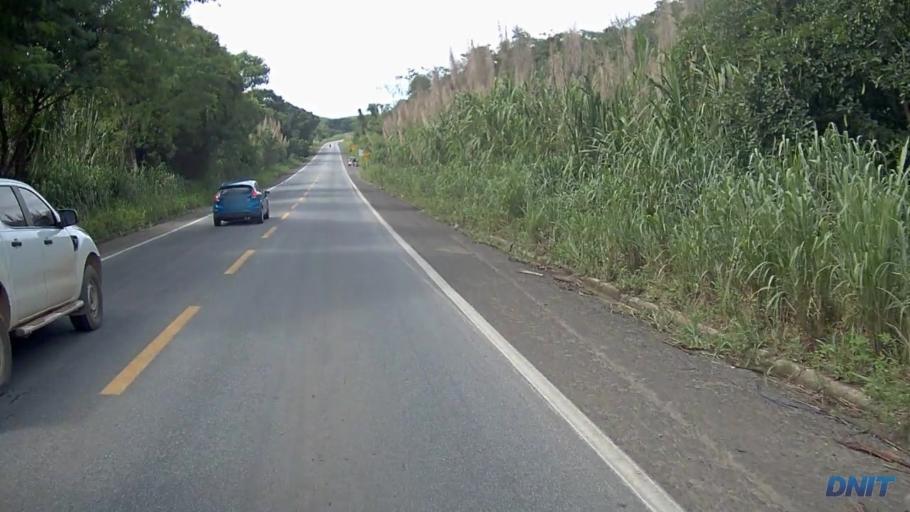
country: BR
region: Minas Gerais
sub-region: Ipaba
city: Ipaba
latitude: -19.3499
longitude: -42.4335
